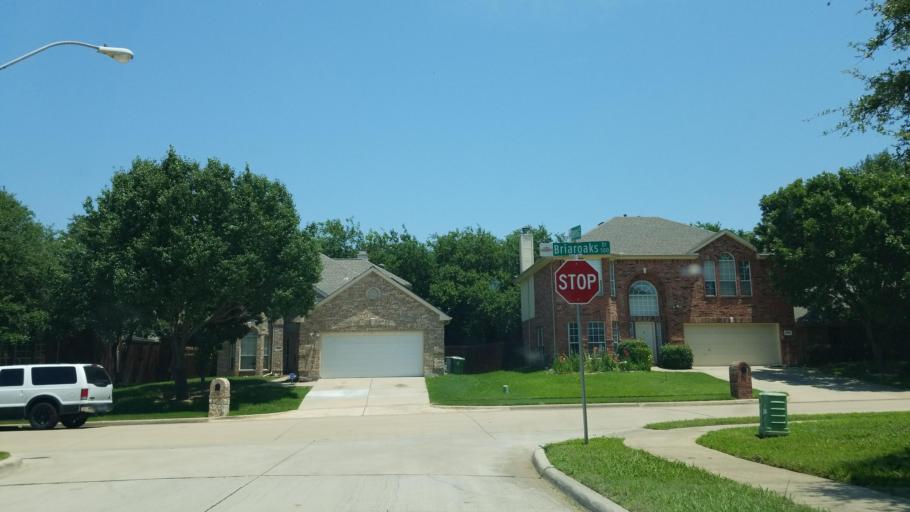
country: US
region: Texas
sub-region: Denton County
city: Hickory Creek
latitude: 33.1322
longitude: -97.0360
